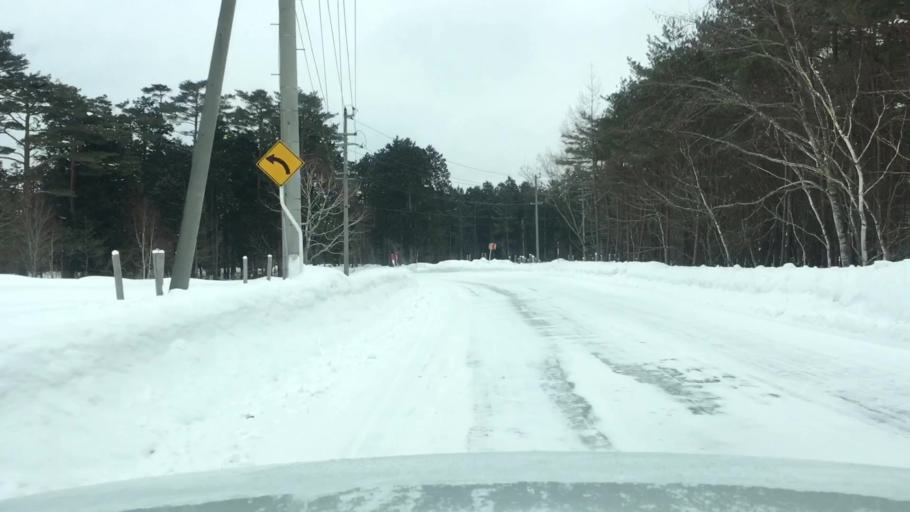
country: JP
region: Iwate
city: Shizukuishi
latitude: 39.9823
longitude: 141.0031
